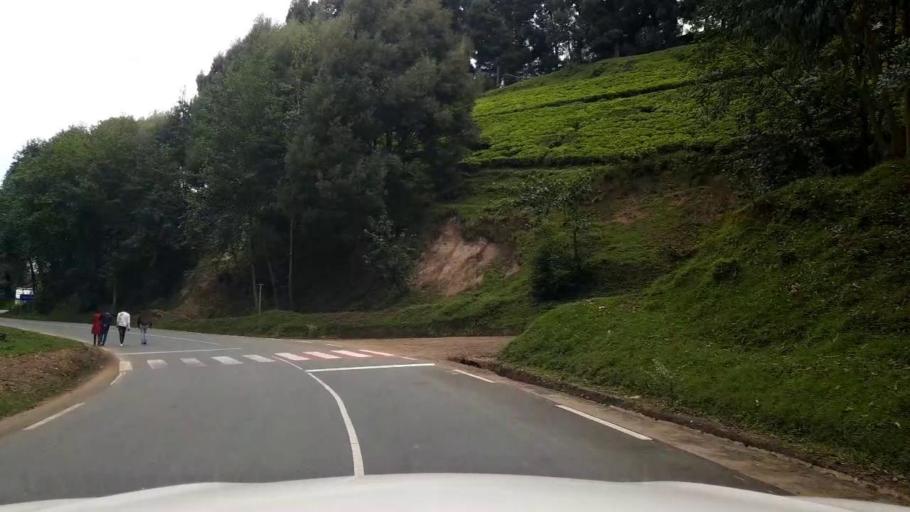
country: RW
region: Northern Province
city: Musanze
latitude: -1.6587
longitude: 29.5109
